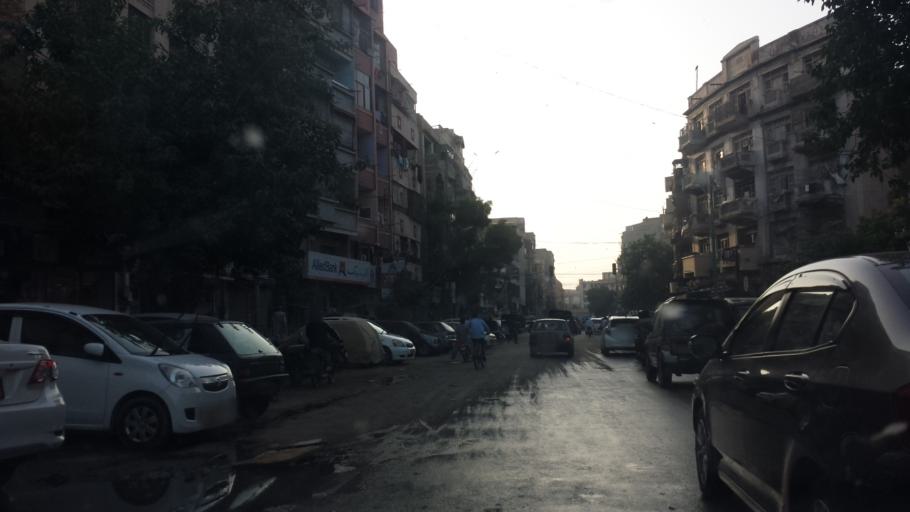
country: PK
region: Sindh
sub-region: Karachi District
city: Karachi
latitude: 24.8542
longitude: 67.0120
